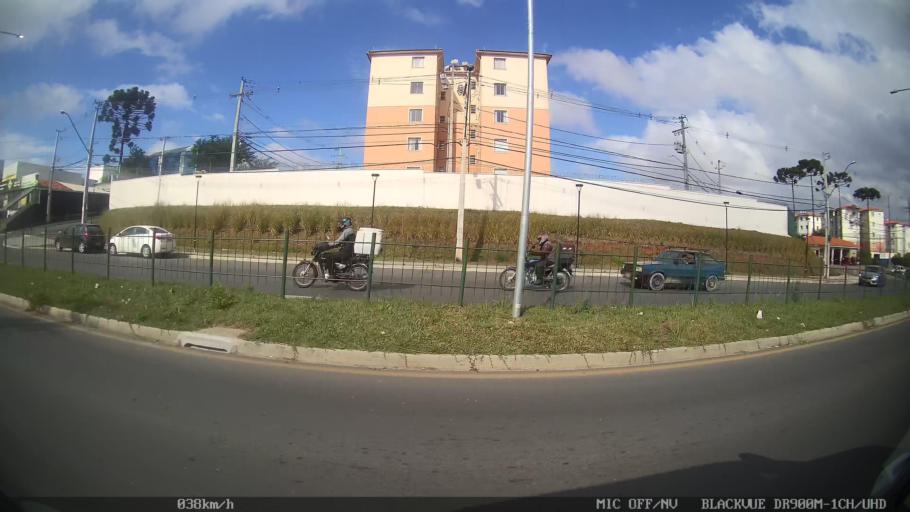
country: BR
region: Parana
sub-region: Pinhais
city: Pinhais
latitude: -25.3852
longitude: -49.1881
